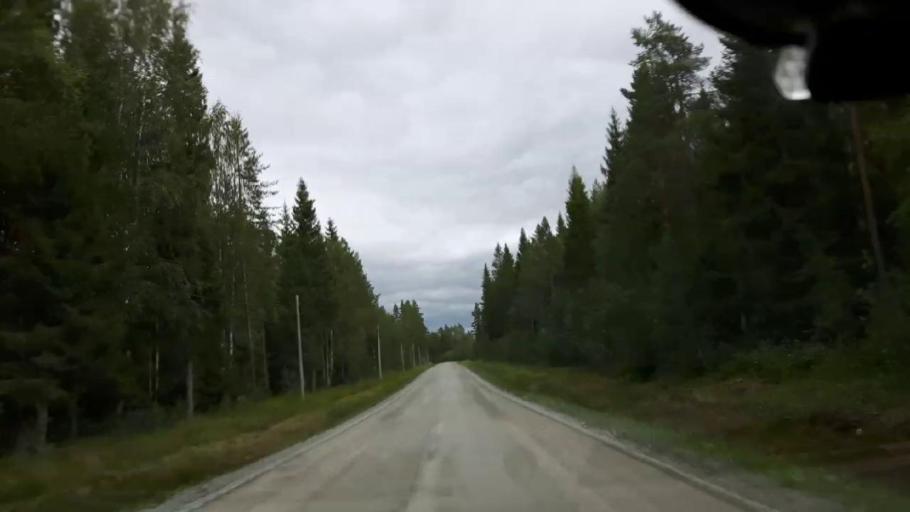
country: SE
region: Jaemtland
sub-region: OEstersunds Kommun
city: Brunflo
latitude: 63.1074
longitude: 15.0363
